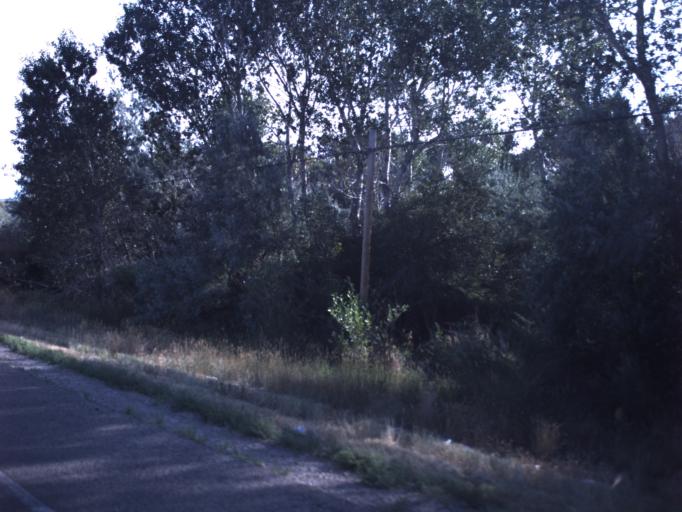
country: US
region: Utah
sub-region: Uintah County
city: Vernal
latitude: 40.4818
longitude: -109.5290
